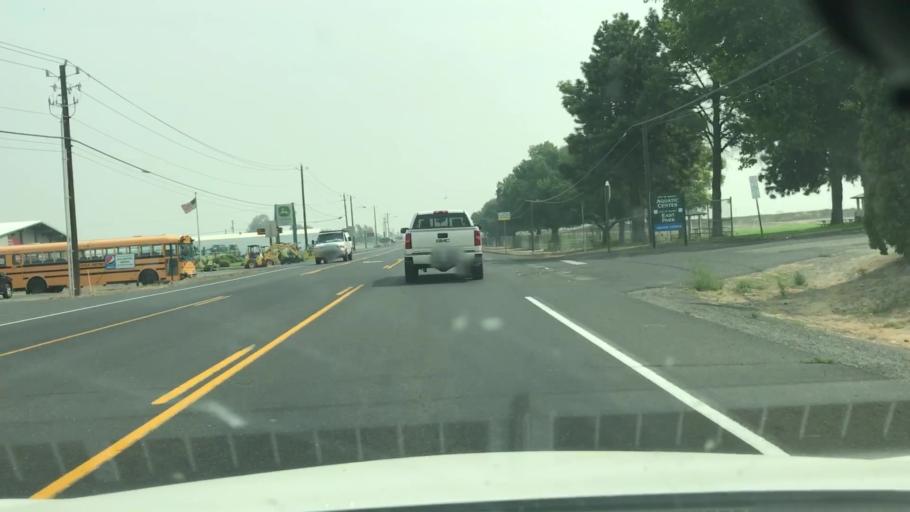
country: US
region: Washington
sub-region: Grant County
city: Quincy
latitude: 47.2340
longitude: -119.8396
